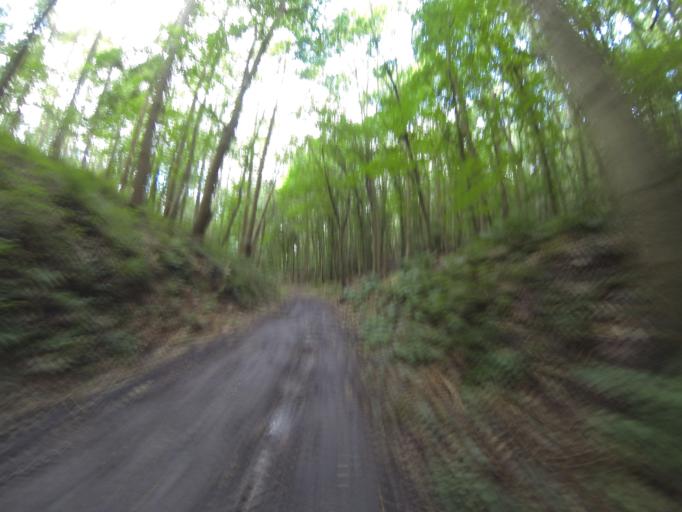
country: GB
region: England
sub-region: Greater London
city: Bexley
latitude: 51.4295
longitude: 0.1534
